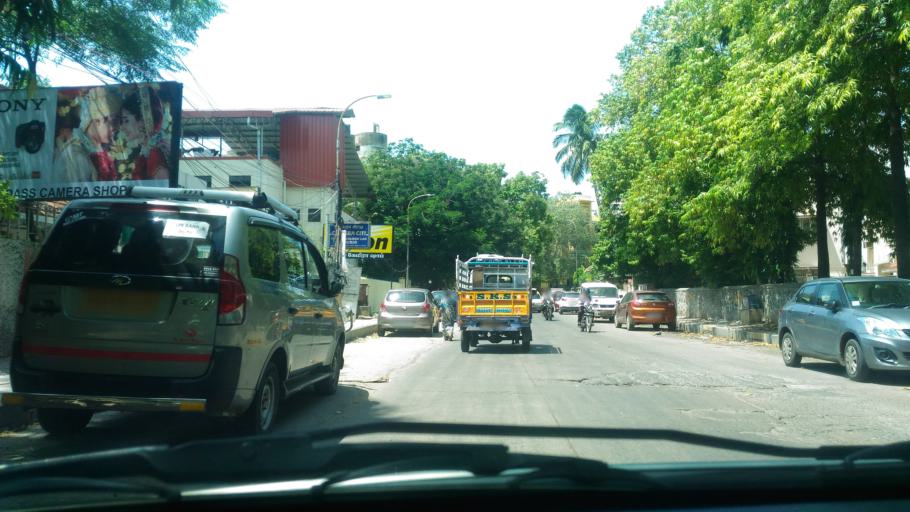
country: IN
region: Tamil Nadu
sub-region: Chennai
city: Chetput
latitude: 13.0496
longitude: 80.2456
